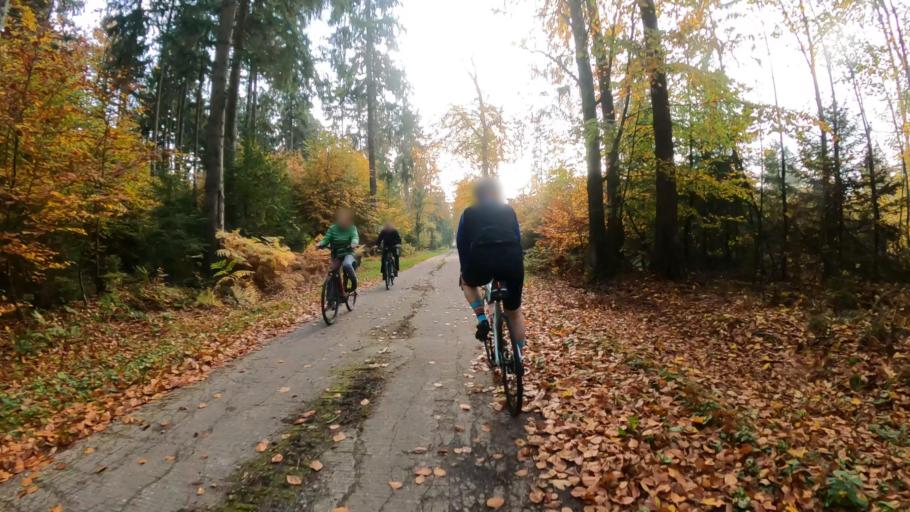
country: DE
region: Lower Saxony
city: Buchholz in der Nordheide
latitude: 53.3534
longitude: 9.8218
